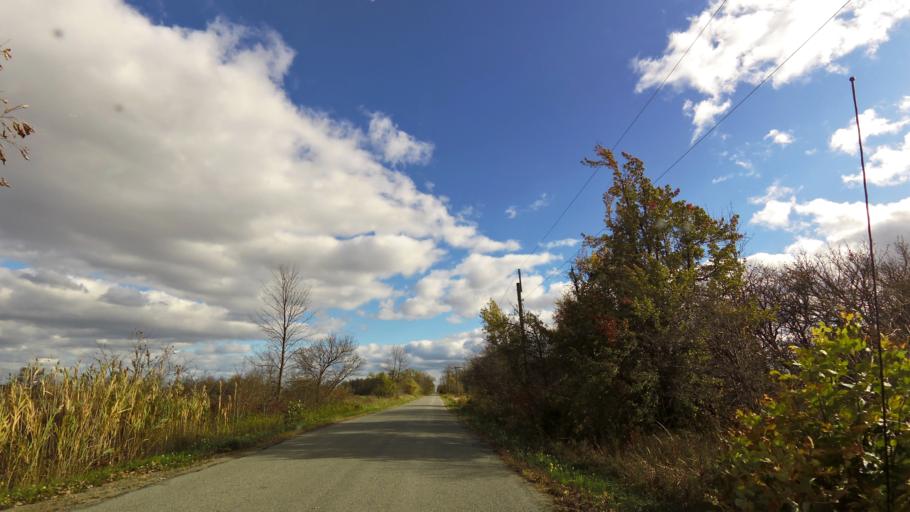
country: CA
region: Ontario
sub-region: Halton
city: Milton
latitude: 43.4555
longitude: -79.8645
